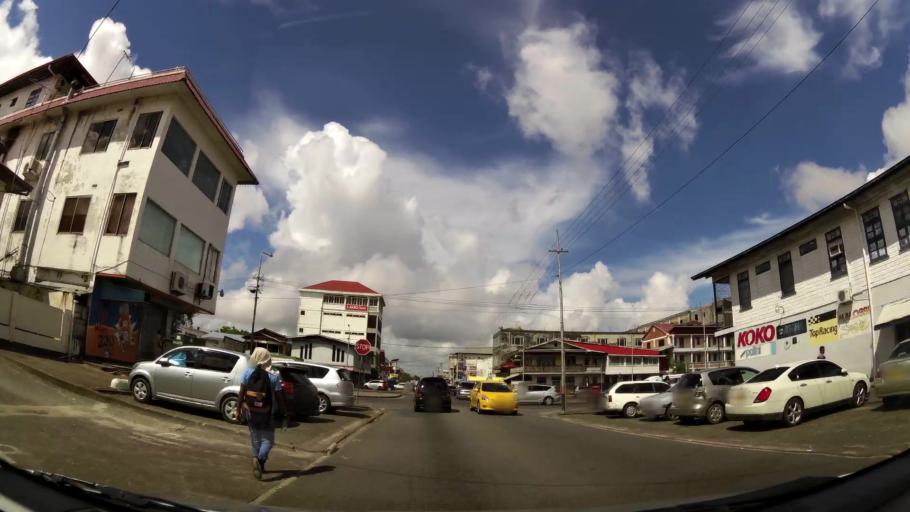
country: SR
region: Paramaribo
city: Paramaribo
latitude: 5.8267
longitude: -55.1650
